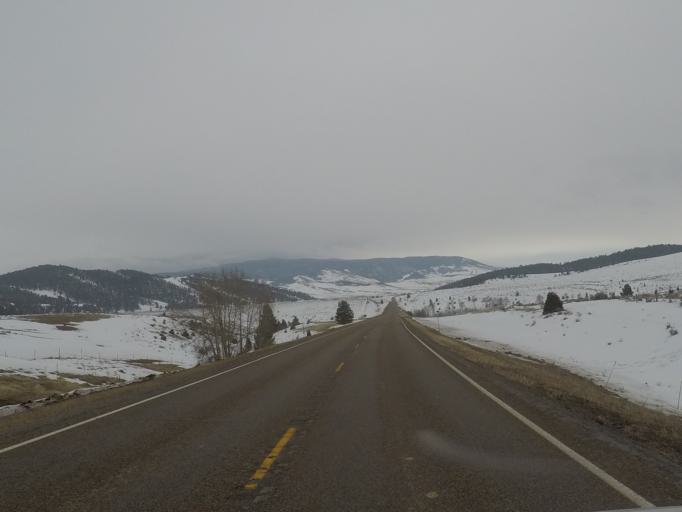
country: US
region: Montana
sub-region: Meagher County
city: White Sulphur Springs
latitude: 46.6282
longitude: -110.8488
